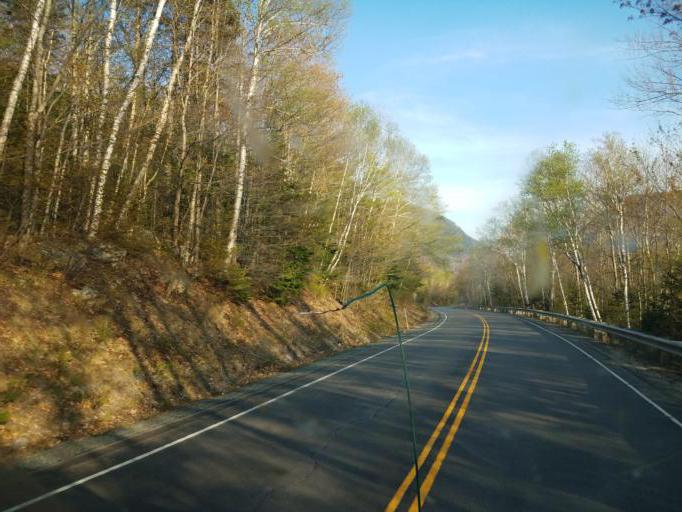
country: US
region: New Hampshire
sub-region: Grafton County
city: Woodstock
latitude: 44.0385
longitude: -71.5227
